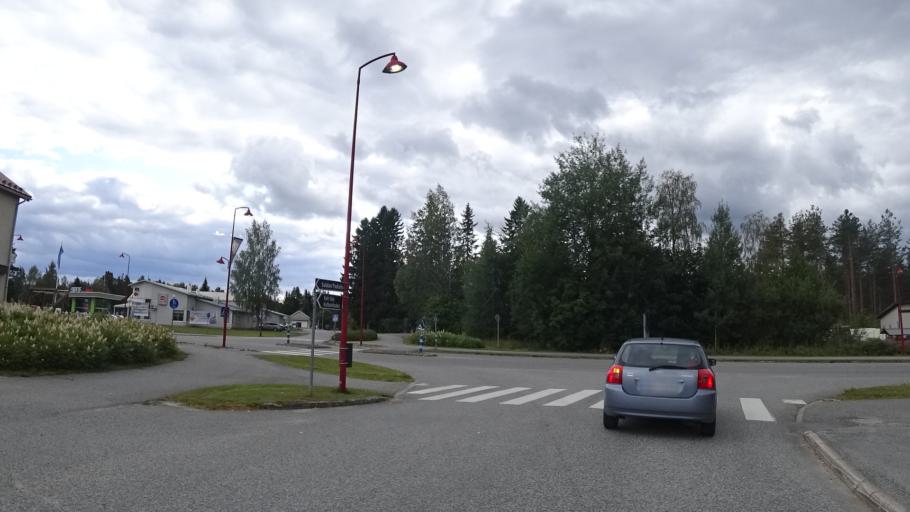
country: FI
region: North Karelia
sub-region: Joensuu
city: Ilomantsi
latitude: 62.6692
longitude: 30.9377
